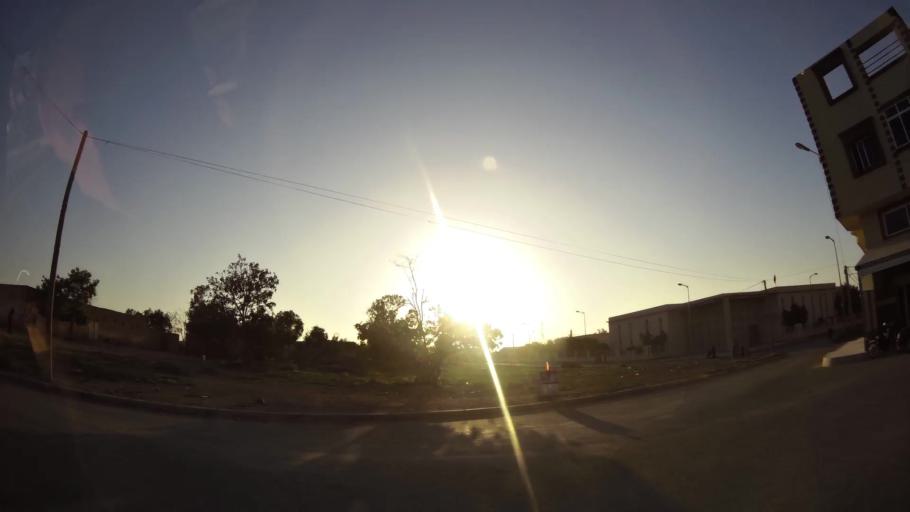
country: MA
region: Oriental
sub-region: Oujda-Angad
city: Oujda
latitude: 34.7137
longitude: -1.9083
